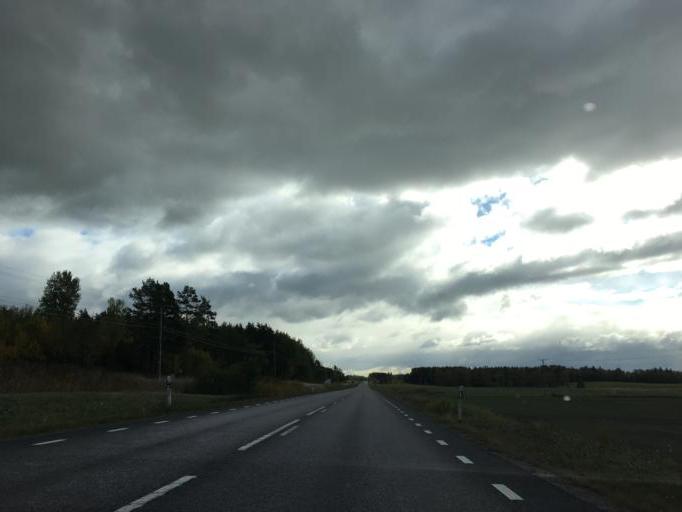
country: SE
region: Soedermanland
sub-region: Nykopings Kommun
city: Olstorp
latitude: 58.8937
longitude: 16.6522
